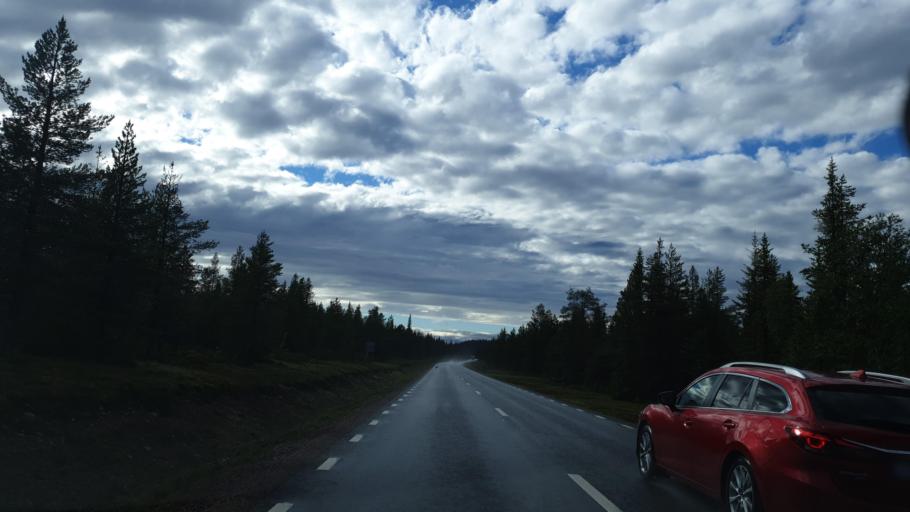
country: SE
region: Norrbotten
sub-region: Arjeplogs Kommun
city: Arjeplog
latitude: 65.9104
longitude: 18.3439
